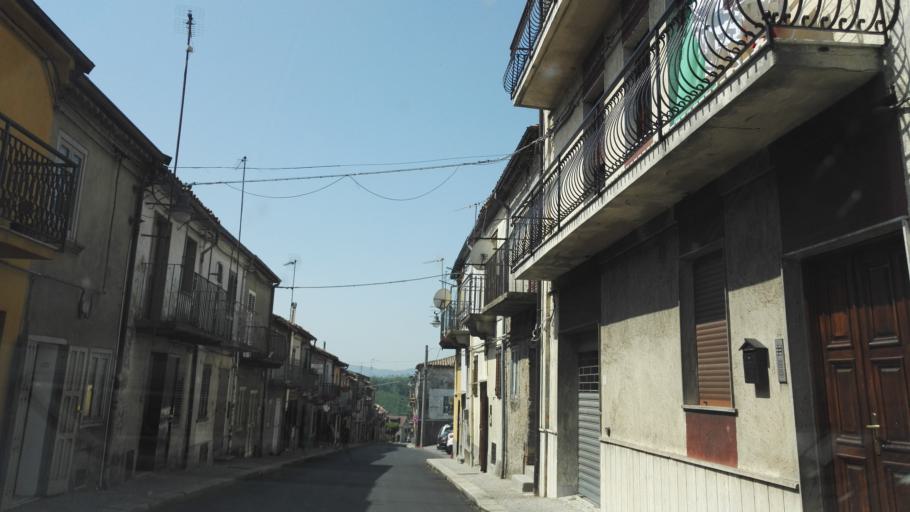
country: IT
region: Calabria
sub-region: Provincia di Vibo-Valentia
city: Mongiana
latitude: 38.5151
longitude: 16.3202
